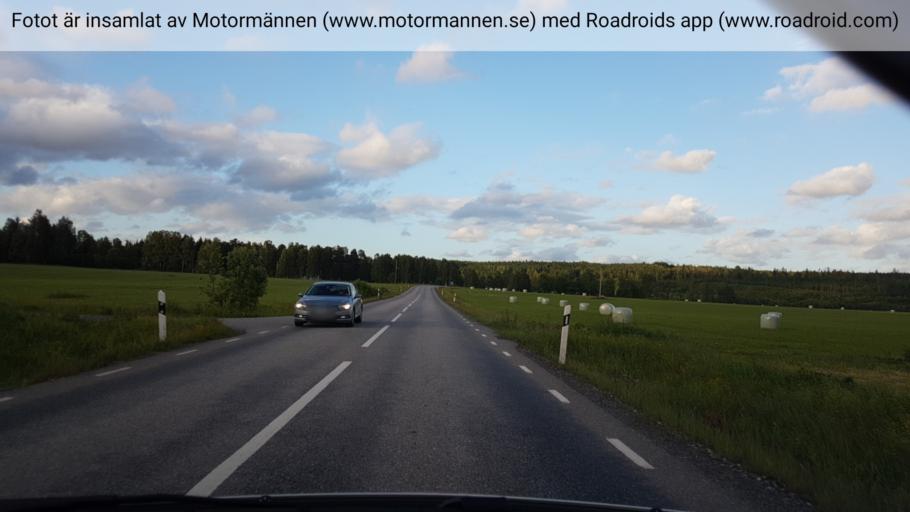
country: SE
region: OErebro
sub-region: Nora Kommun
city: As
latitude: 59.4541
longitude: 14.8818
